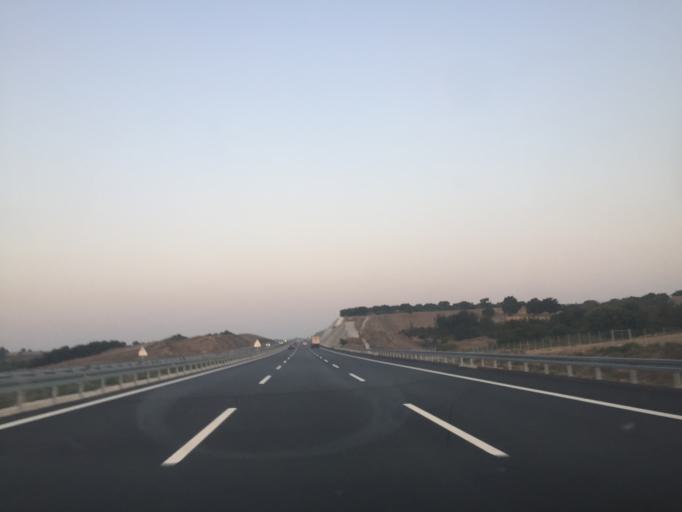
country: TR
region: Bursa
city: Mahmudiye
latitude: 40.2626
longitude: 28.6706
